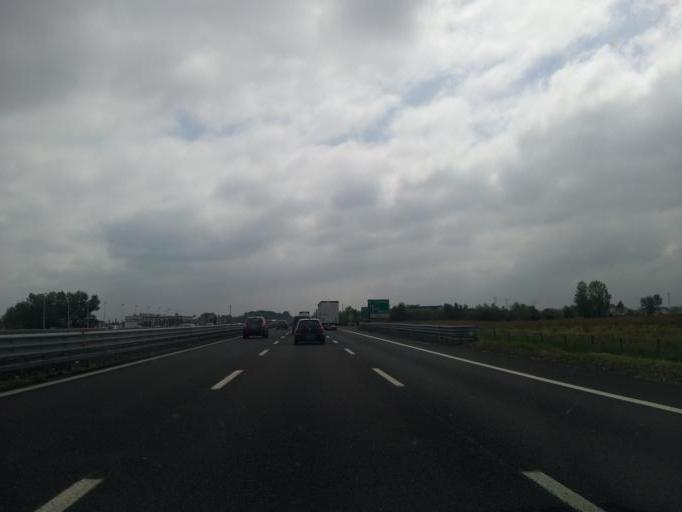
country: IT
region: Veneto
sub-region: Provincia di Vicenza
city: Torri di Quartesolo
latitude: 45.5157
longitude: 11.5872
